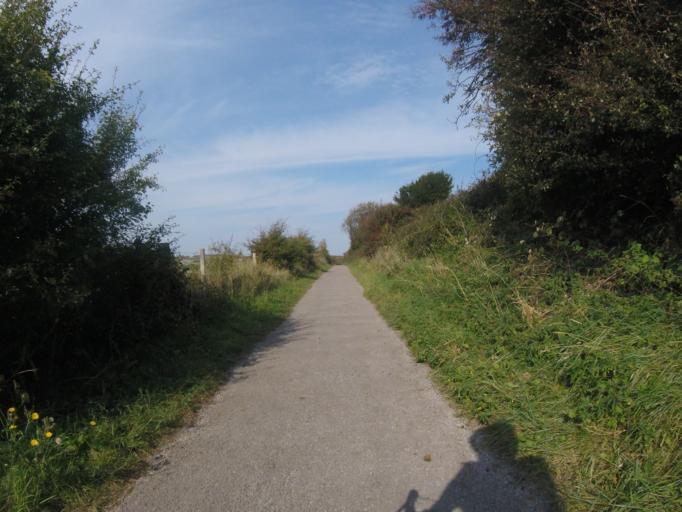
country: GB
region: England
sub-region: East Sussex
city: Portslade
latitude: 50.8643
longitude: -0.2010
